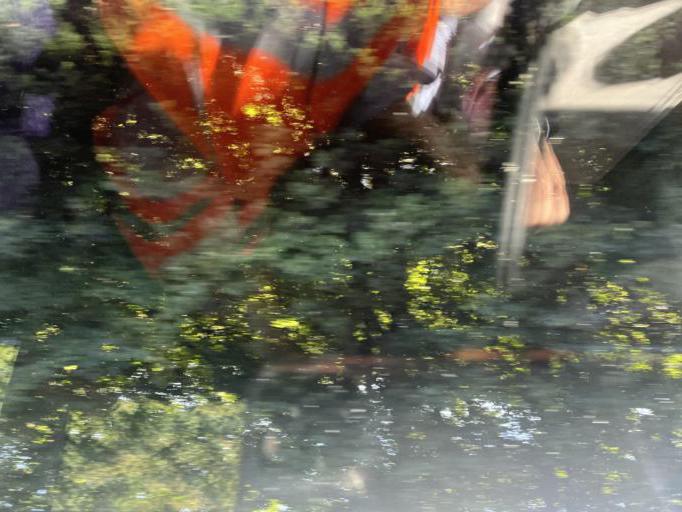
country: GB
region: England
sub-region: Lincolnshire
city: Donington
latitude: 52.9703
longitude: -0.1823
